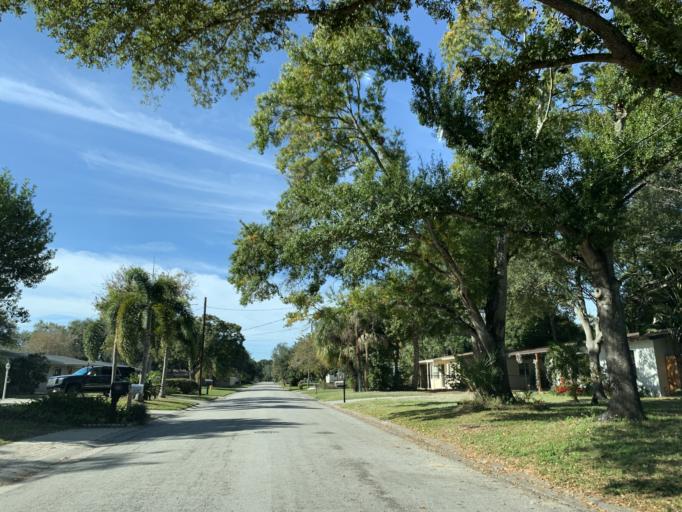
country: US
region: Florida
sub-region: Hillsborough County
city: Tampa
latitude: 27.8852
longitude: -82.4961
